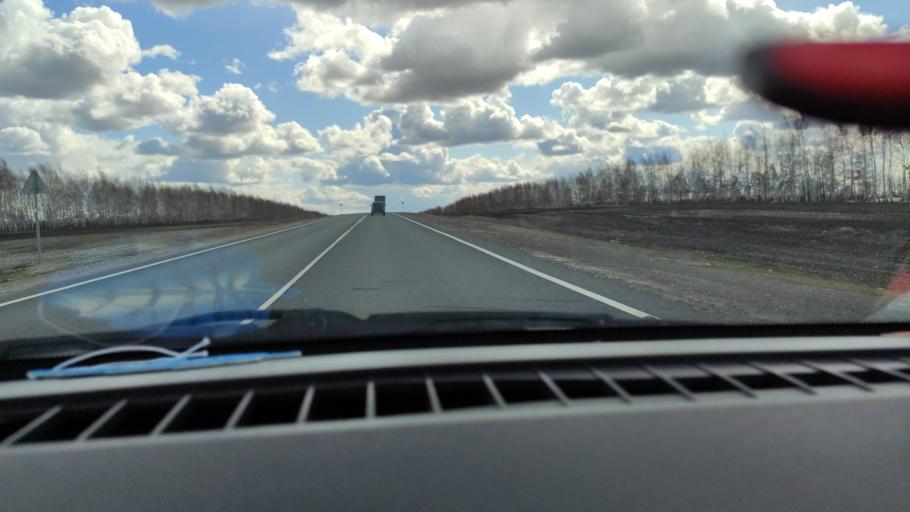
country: RU
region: Samara
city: Syzran'
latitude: 52.9085
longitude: 48.2988
